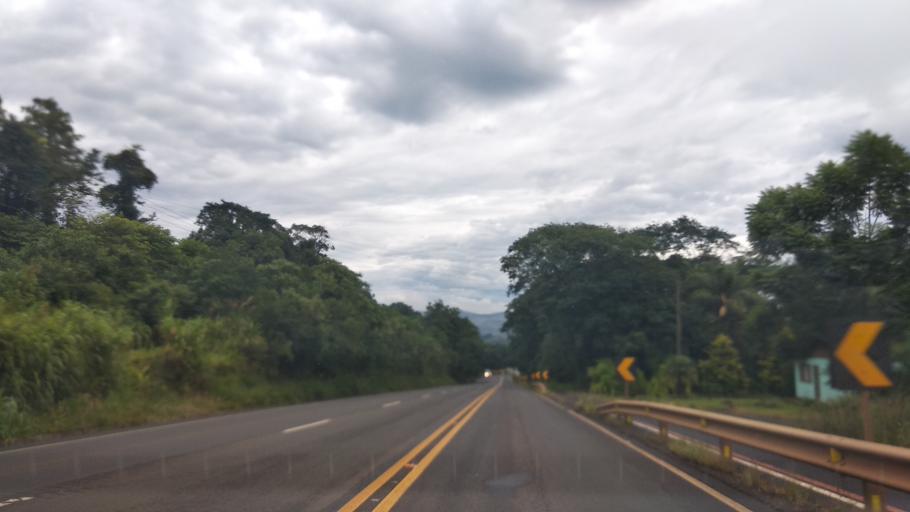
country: BR
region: Santa Catarina
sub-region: Videira
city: Videira
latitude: -27.0816
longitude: -51.2374
